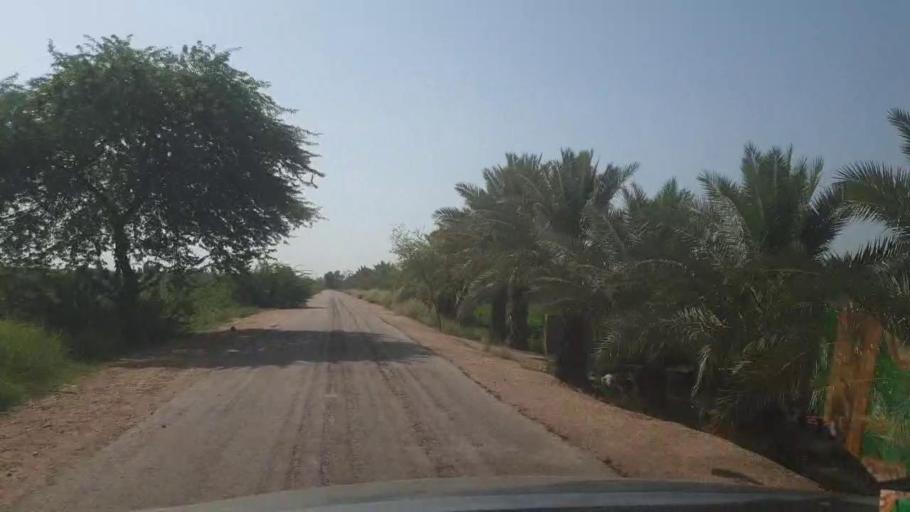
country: PK
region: Sindh
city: Rohri
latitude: 27.4638
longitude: 69.0401
